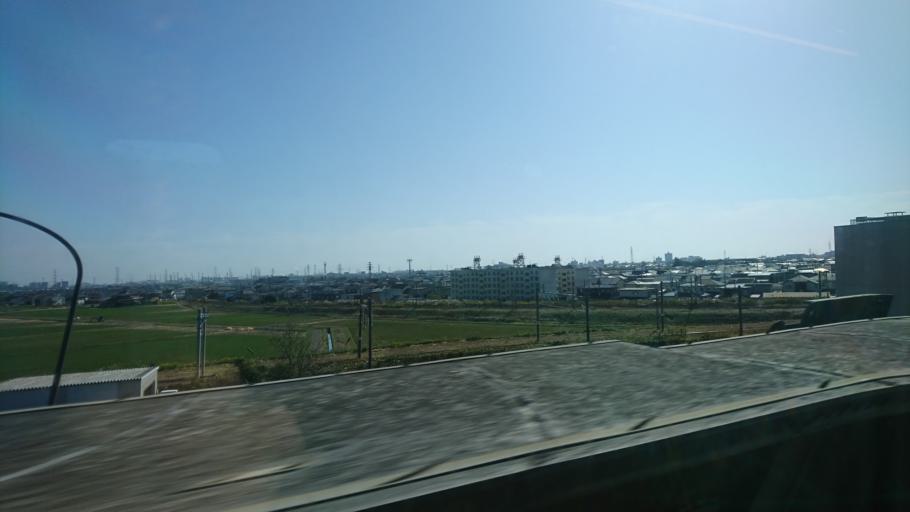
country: JP
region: Miyagi
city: Rifu
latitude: 38.3029
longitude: 140.9582
